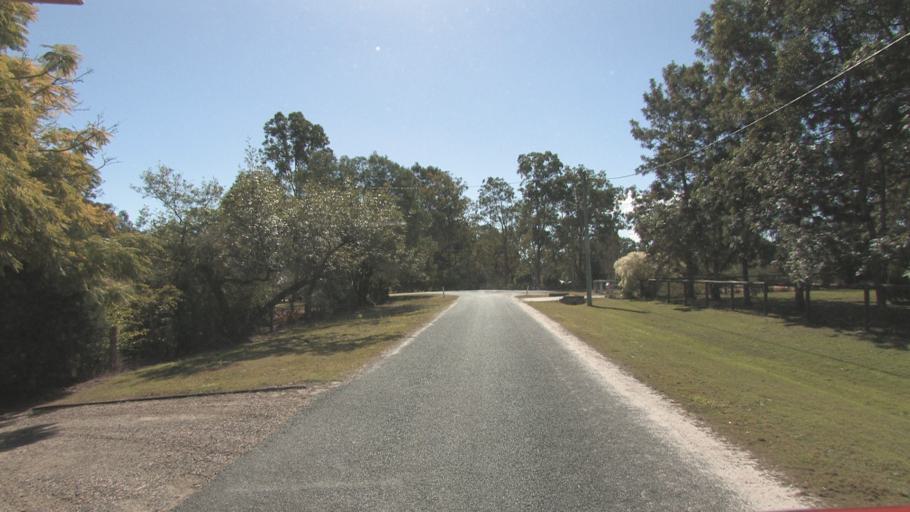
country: AU
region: Queensland
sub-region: Logan
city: Chambers Flat
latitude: -27.7464
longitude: 153.0975
